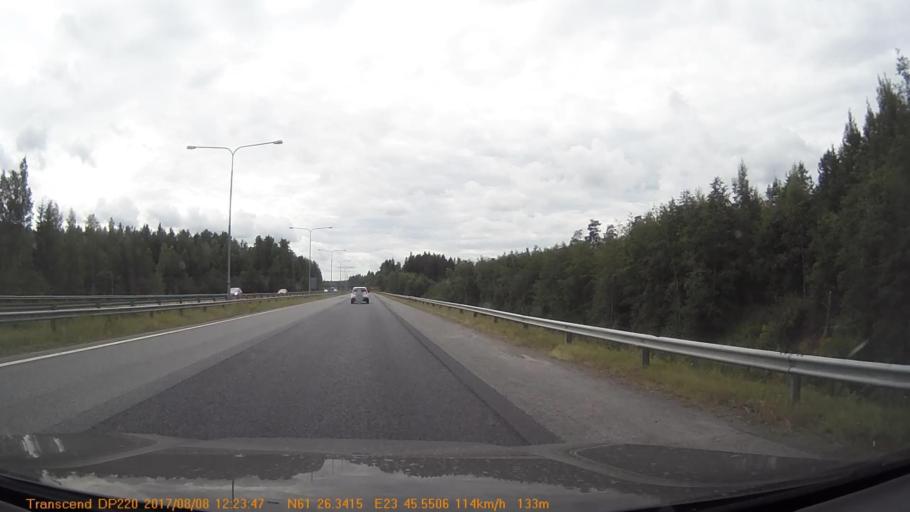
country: FI
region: Pirkanmaa
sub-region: Tampere
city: Tampere
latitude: 61.4387
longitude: 23.7590
